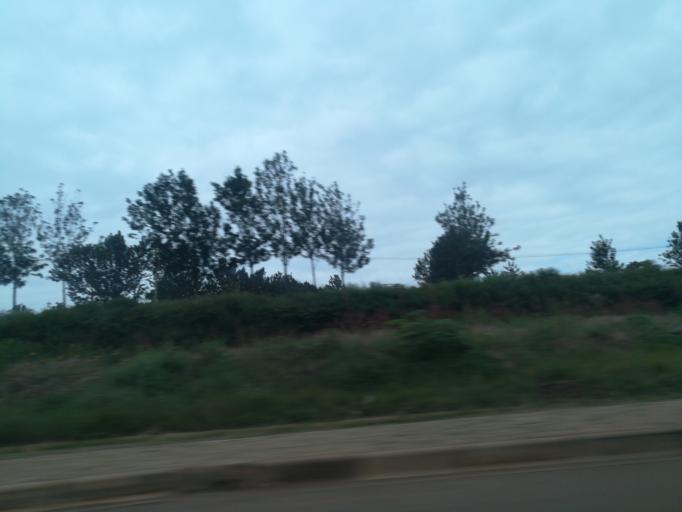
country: KE
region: Nairobi Area
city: Thika
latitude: -1.0818
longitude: 37.0425
